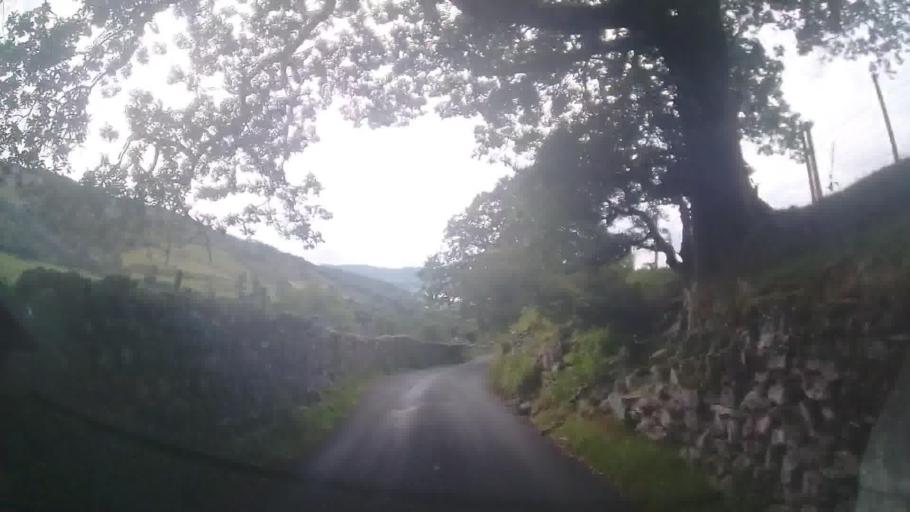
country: GB
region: England
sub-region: Cumbria
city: Ambleside
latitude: 54.4387
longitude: -2.9504
